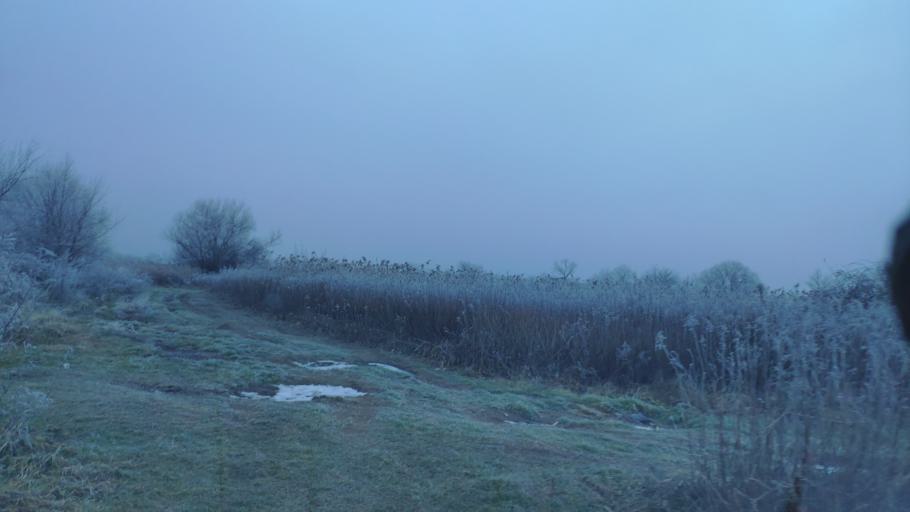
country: SK
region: Kosicky
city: Kosice
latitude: 48.6181
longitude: 21.3314
